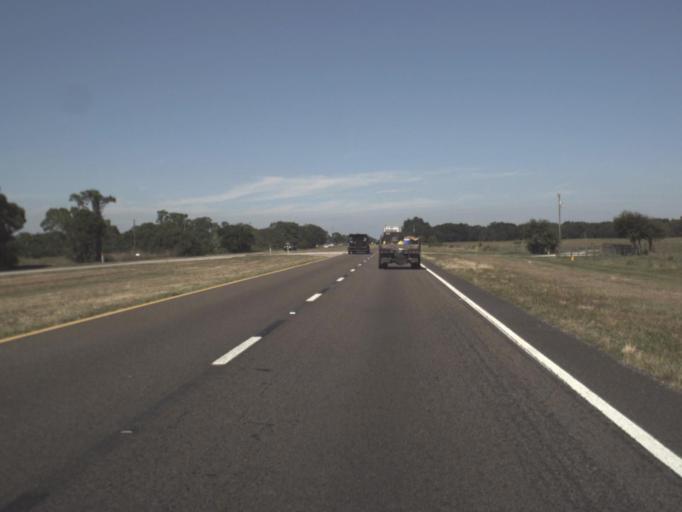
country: US
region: Florida
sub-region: Highlands County
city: Placid Lakes
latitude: 27.0796
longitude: -81.3349
